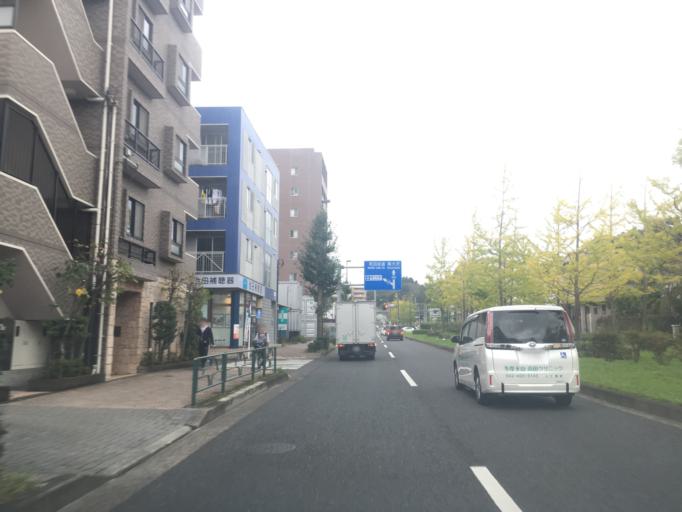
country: JP
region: Tokyo
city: Hino
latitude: 35.6249
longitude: 139.4195
